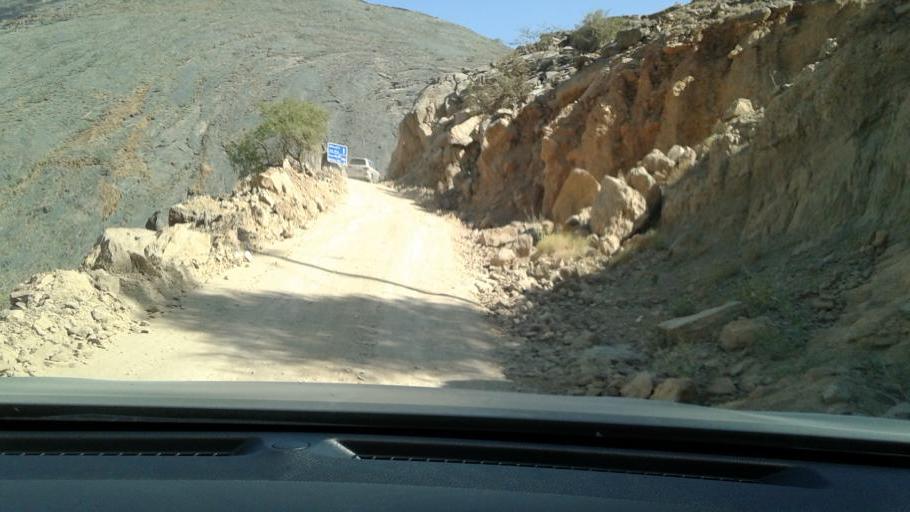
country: OM
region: Al Batinah
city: Bayt al `Awabi
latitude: 23.2048
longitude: 57.3908
